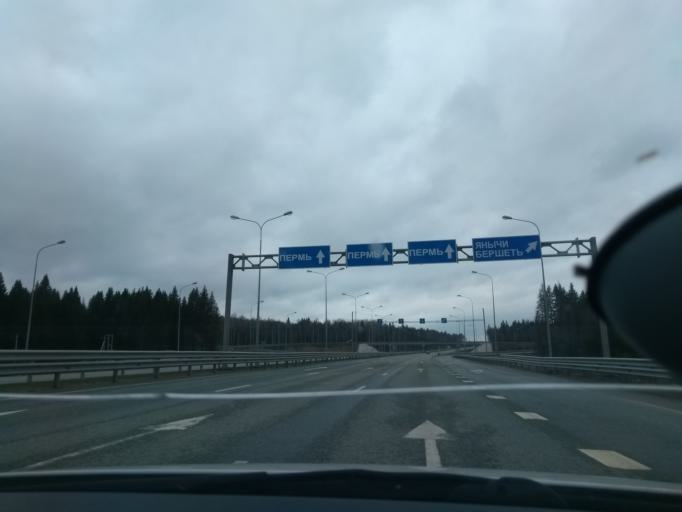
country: RU
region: Perm
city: Bershet'
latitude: 57.6967
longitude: 56.3861
